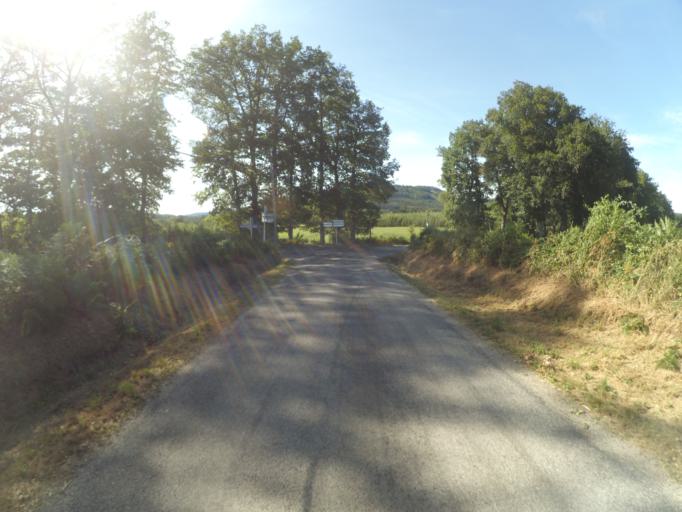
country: FR
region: Limousin
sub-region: Departement de la Haute-Vienne
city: Eymoutiers
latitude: 45.7093
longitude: 1.8622
